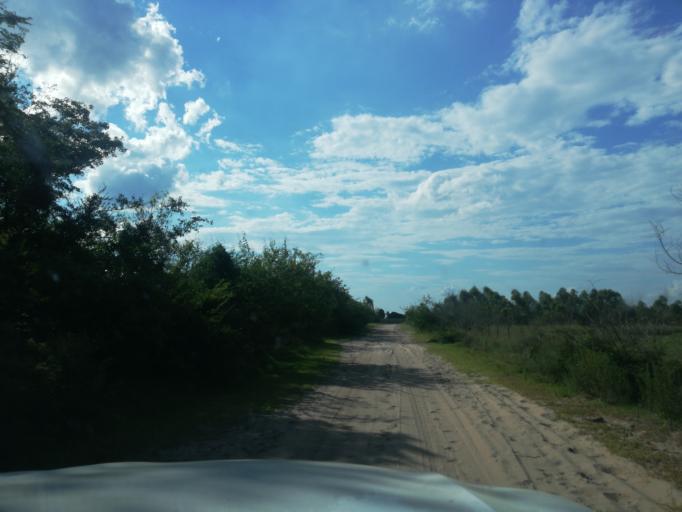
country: AR
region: Corrientes
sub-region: Departamento de San Miguel
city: San Miguel
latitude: -27.9908
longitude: -57.5665
